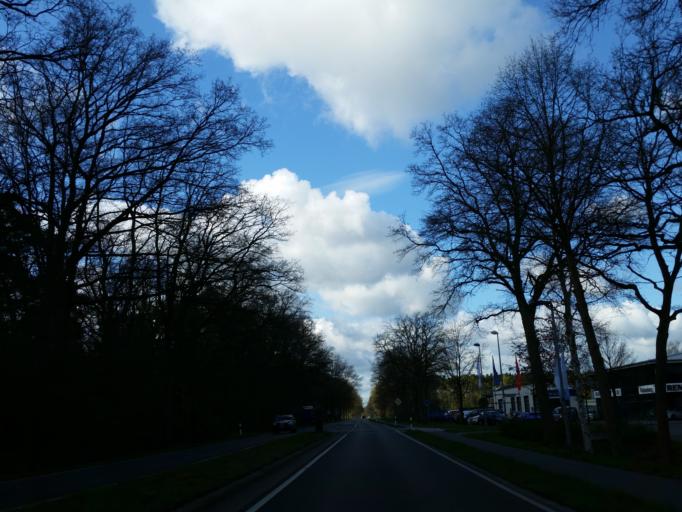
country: DE
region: Lower Saxony
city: Rotenburg
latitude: 53.0948
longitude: 9.3744
